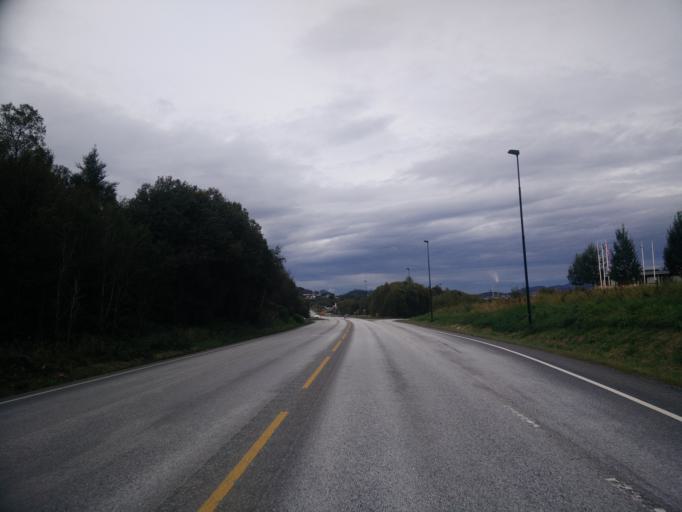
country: NO
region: More og Romsdal
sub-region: Haram
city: Brattvag
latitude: 62.4710
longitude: 6.3706
